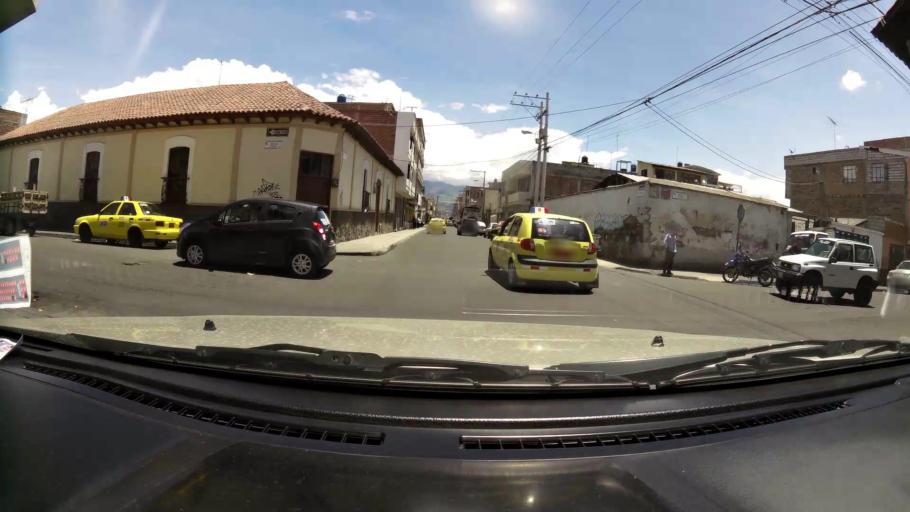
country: EC
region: Chimborazo
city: Riobamba
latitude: -1.6699
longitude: -78.6465
